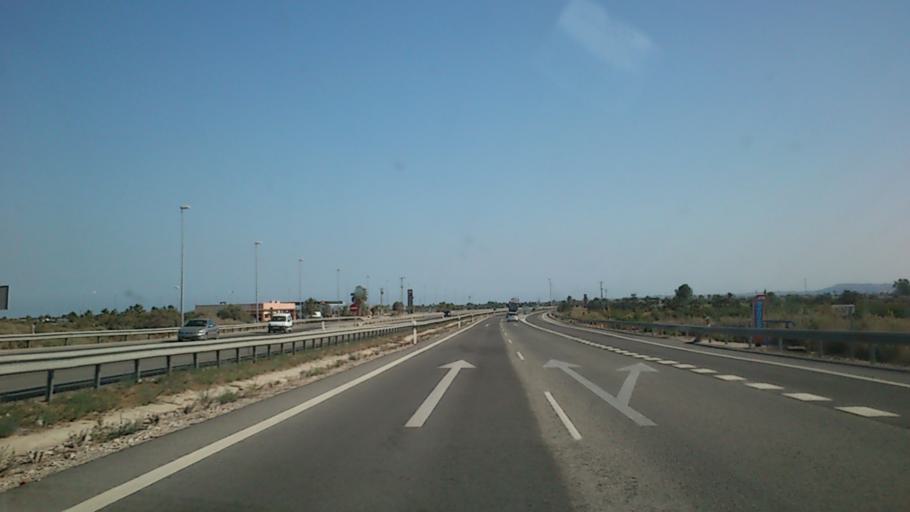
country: ES
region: Valencia
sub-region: Provincia de Alicante
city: San Isidro
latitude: 38.1987
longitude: -0.8145
